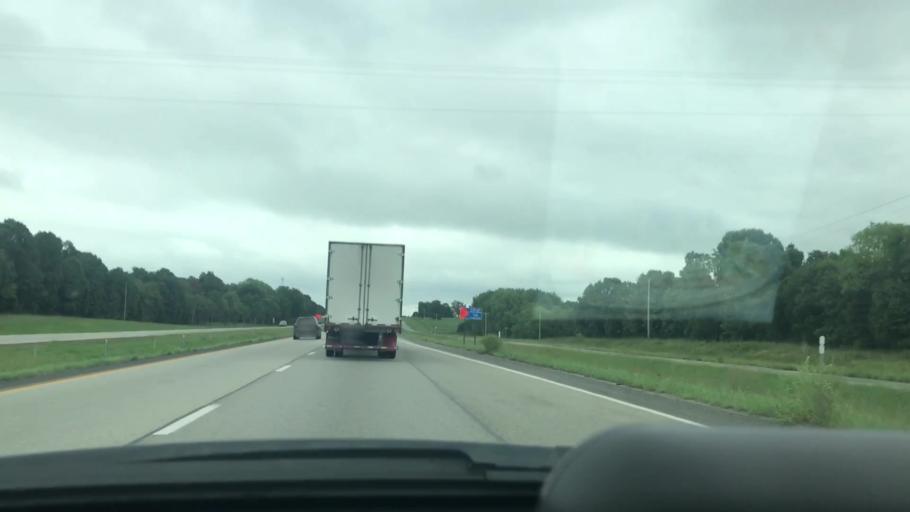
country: US
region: Missouri
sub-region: Greene County
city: Republic
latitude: 37.1858
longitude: -93.5651
